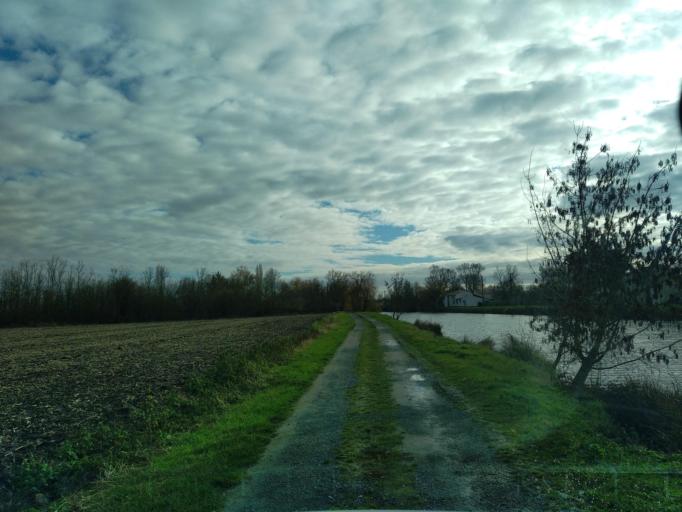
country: FR
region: Pays de la Loire
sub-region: Departement de la Vendee
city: Vix
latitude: 46.3274
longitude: -0.8047
